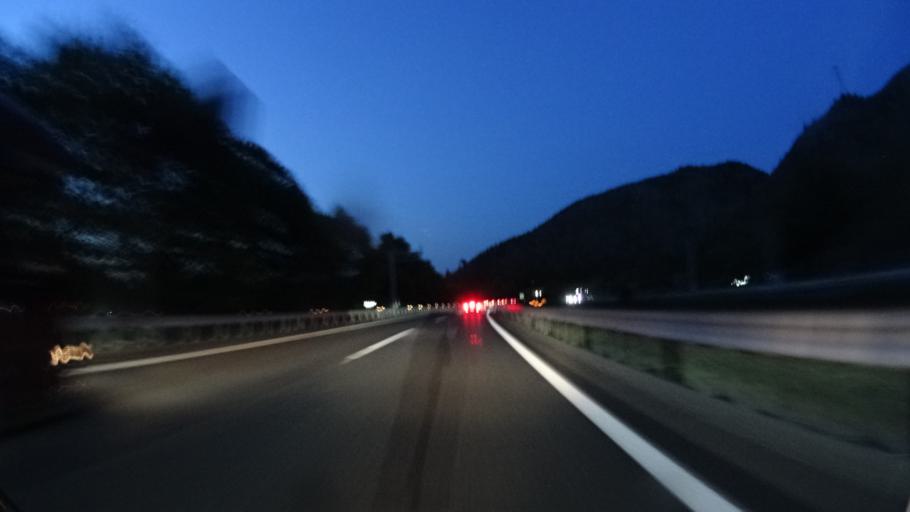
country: JP
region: Hyogo
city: Kariya
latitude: 34.7852
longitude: 134.3984
